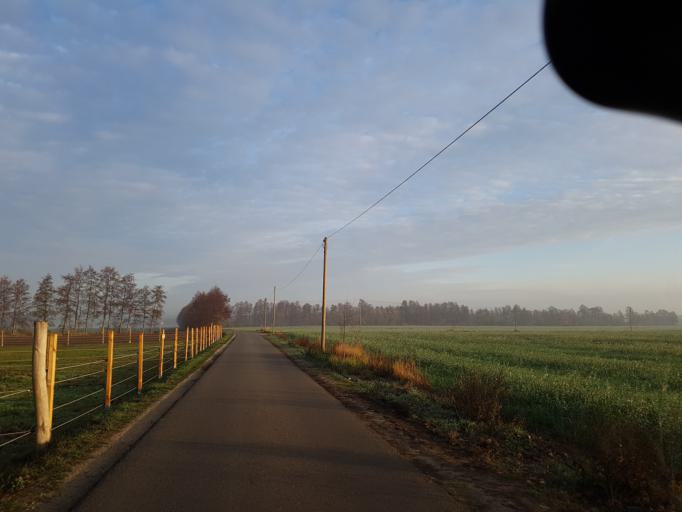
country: DE
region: Saxony-Anhalt
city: Elster
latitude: 51.8669
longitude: 12.8462
